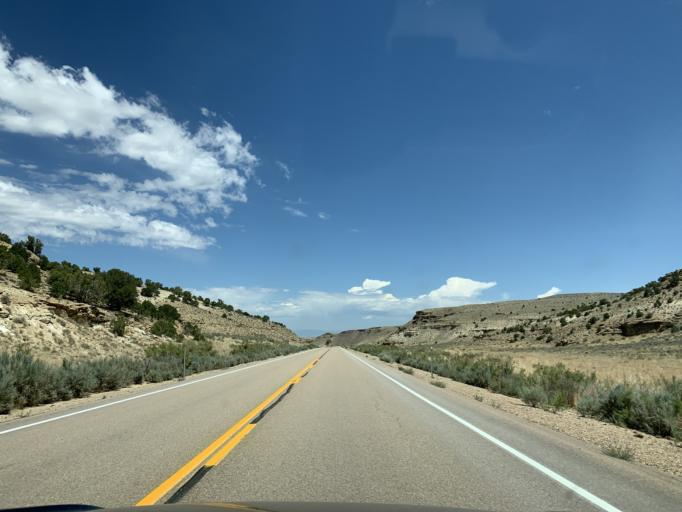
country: US
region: Utah
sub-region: Duchesne County
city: Duchesne
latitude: 39.9934
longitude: -110.1551
